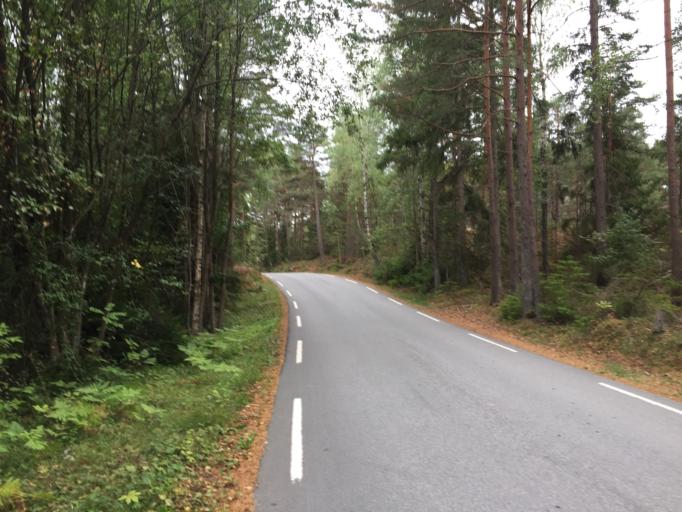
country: NO
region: Ostfold
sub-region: Hvaler
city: Skjaerhalden
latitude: 59.0565
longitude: 11.0357
